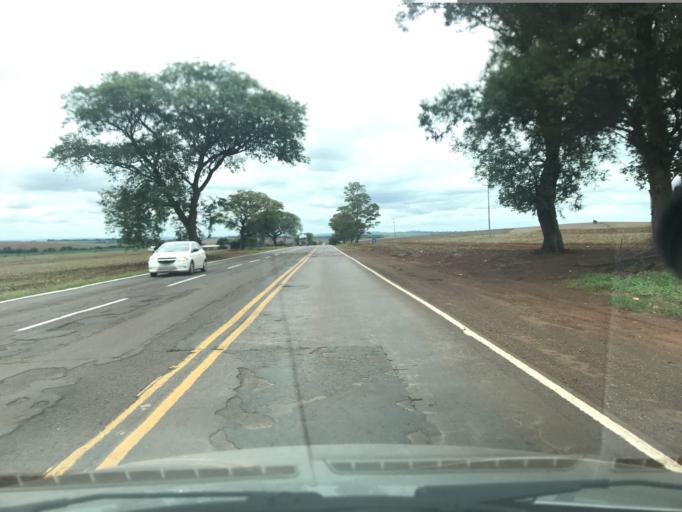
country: BR
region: Parana
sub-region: Terra Boa
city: Terra Boa
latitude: -23.6022
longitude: -52.4047
